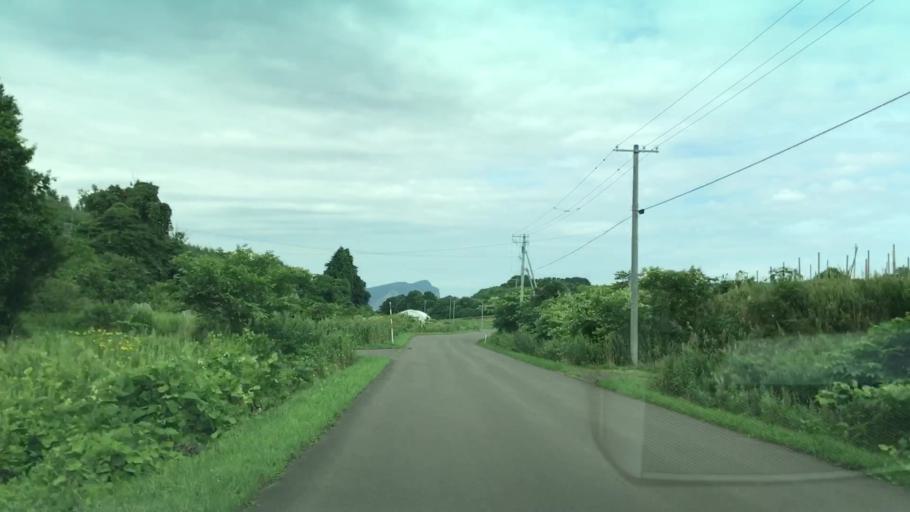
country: JP
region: Hokkaido
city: Yoichi
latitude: 43.1741
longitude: 140.8275
